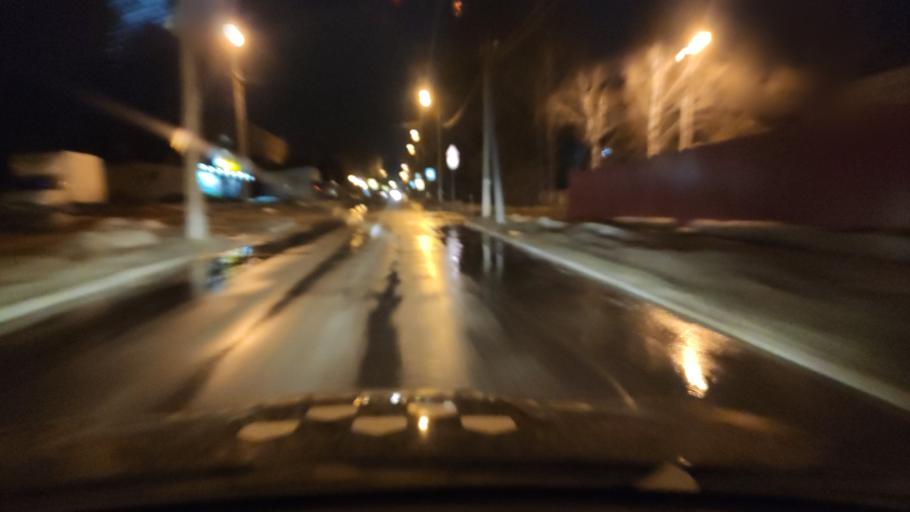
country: RU
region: Samara
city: Povolzhskiy
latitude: 53.5876
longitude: 49.7644
